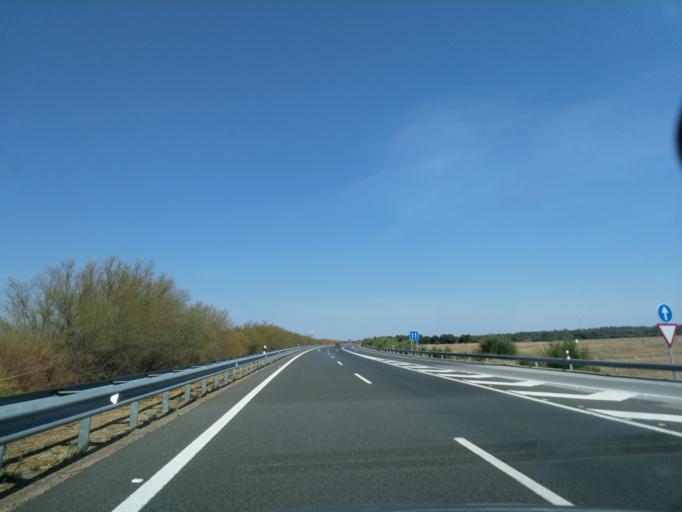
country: ES
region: Extremadura
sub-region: Provincia de Caceres
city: Aldea del Cano
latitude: 39.2912
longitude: -6.3310
